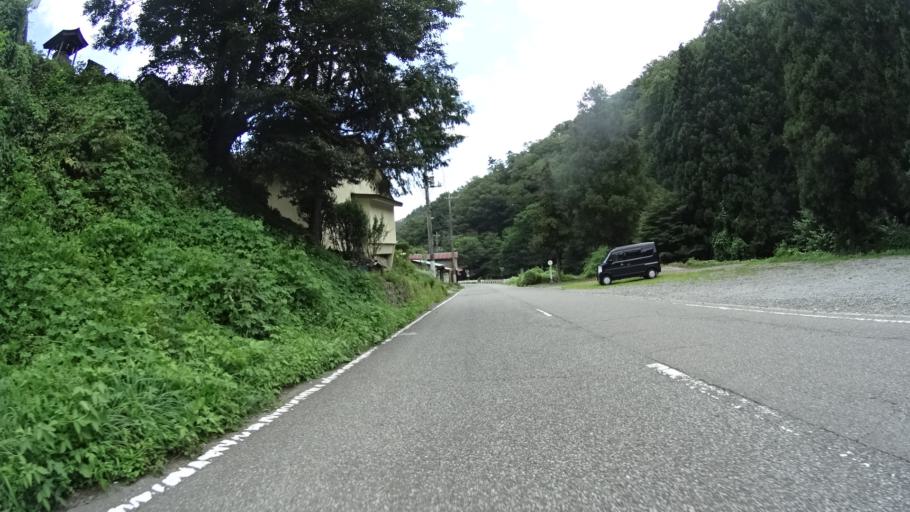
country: JP
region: Yamanashi
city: Kofu-shi
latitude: 35.7622
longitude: 138.5359
